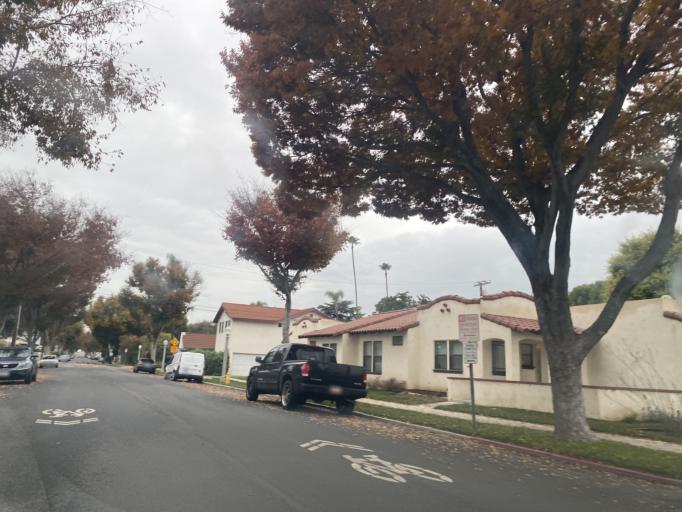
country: US
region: California
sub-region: Orange County
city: Fullerton
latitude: 33.8725
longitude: -117.9109
